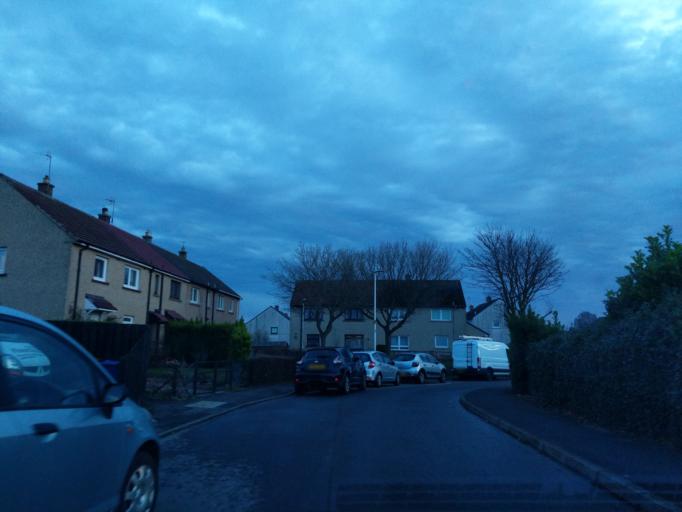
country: GB
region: Scotland
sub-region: Midlothian
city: Loanhead
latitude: 55.8706
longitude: -3.1819
